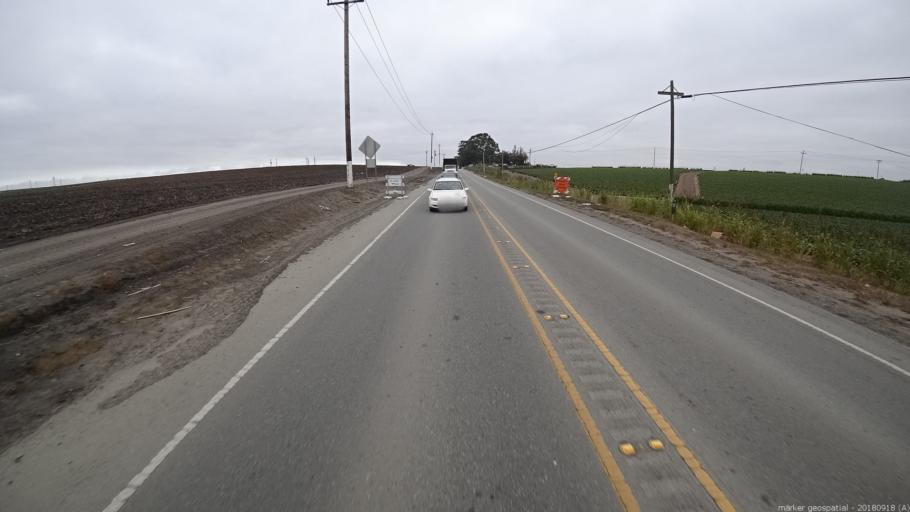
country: US
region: California
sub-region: Monterey County
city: Castroville
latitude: 36.7435
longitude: -121.7302
